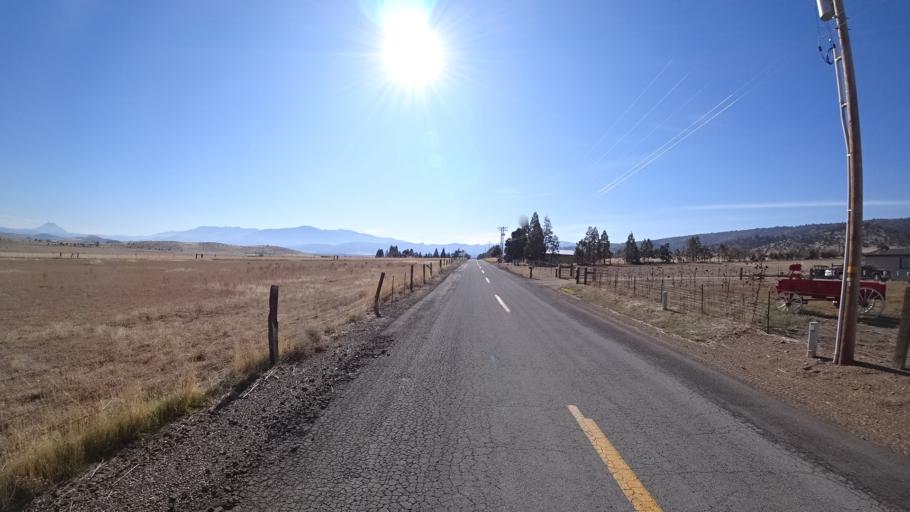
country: US
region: California
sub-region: Siskiyou County
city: Montague
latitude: 41.5961
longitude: -122.5398
